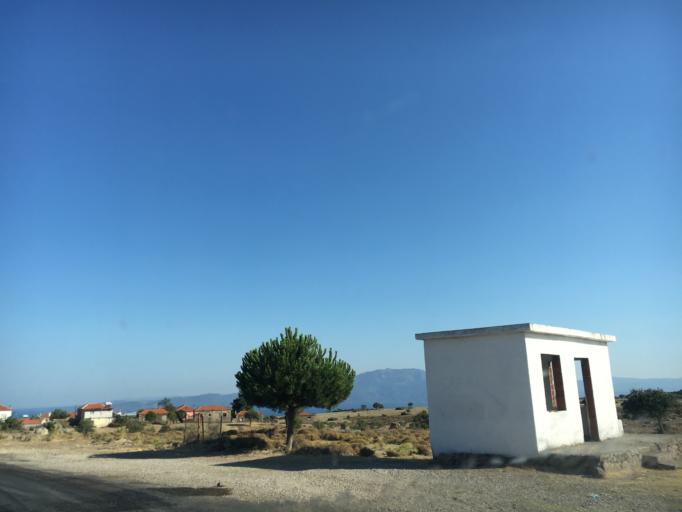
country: TR
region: Canakkale
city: Behram
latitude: 39.5068
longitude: 26.2519
